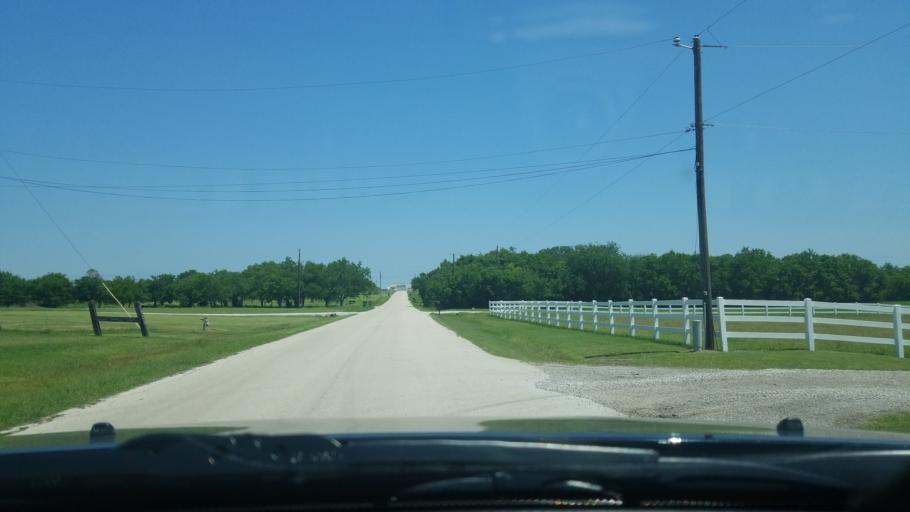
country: US
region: Texas
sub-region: Denton County
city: Krum
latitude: 33.2397
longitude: -97.2590
